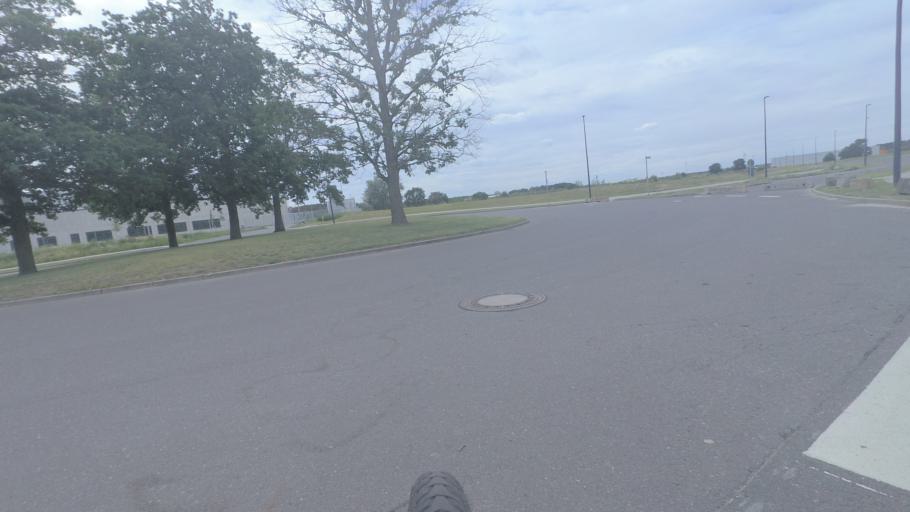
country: DE
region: Brandenburg
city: Grossbeeren
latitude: 52.3196
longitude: 13.3031
